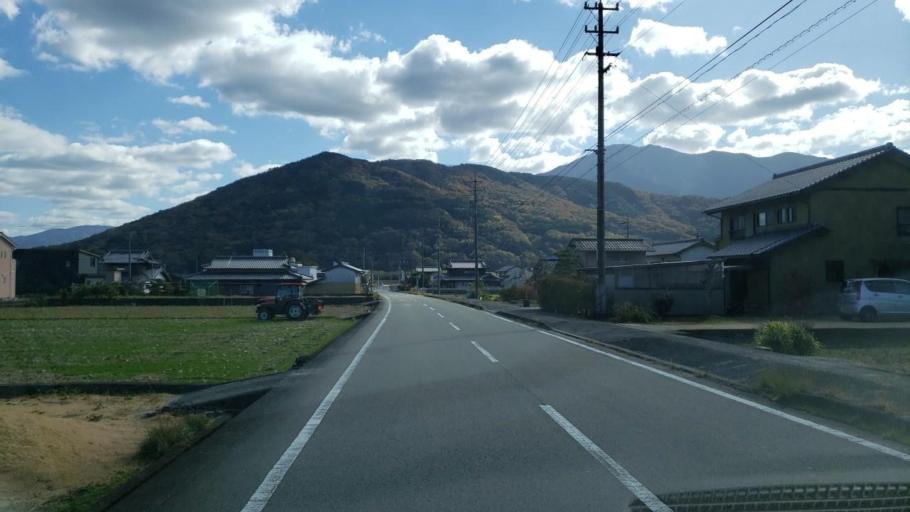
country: JP
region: Tokushima
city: Wakimachi
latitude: 34.0700
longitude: 134.1801
